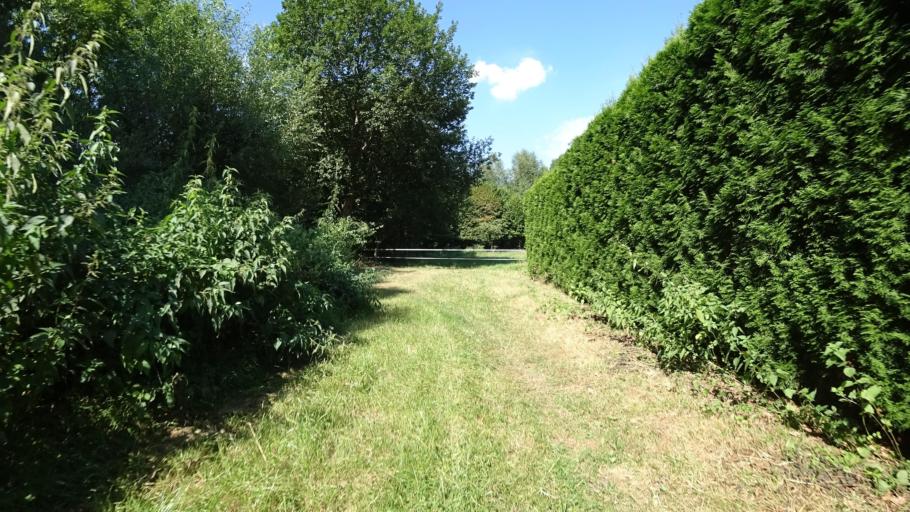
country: DE
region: North Rhine-Westphalia
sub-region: Regierungsbezirk Detmold
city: Steinhagen
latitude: 51.9493
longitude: 8.4659
